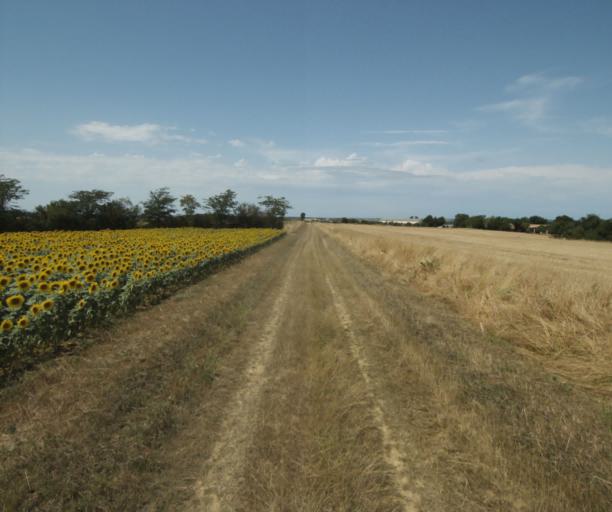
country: FR
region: Midi-Pyrenees
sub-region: Departement de la Haute-Garonne
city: Saint-Felix-Lauragais
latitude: 43.4507
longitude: 1.8573
